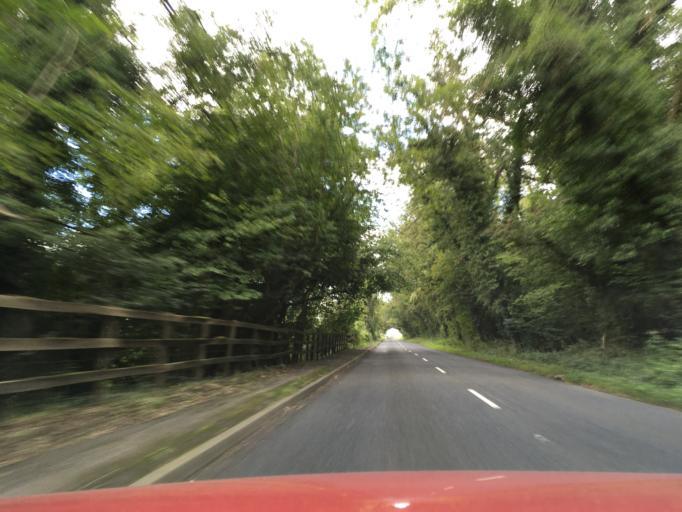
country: GB
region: England
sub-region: Wiltshire
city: Box
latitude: 51.4070
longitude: -2.2399
